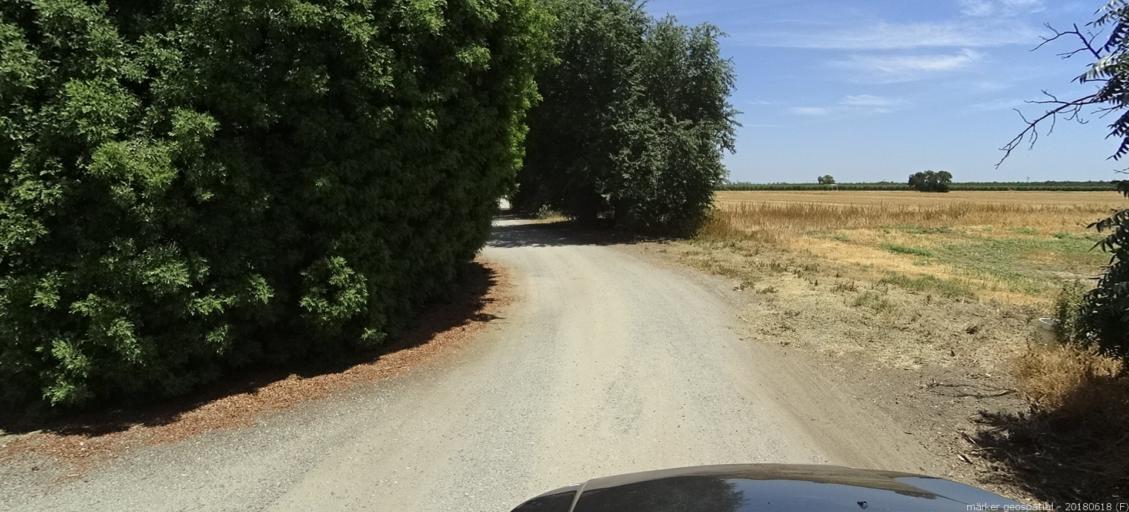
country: US
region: California
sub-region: Madera County
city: Parkwood
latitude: 36.9129
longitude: -120.0949
